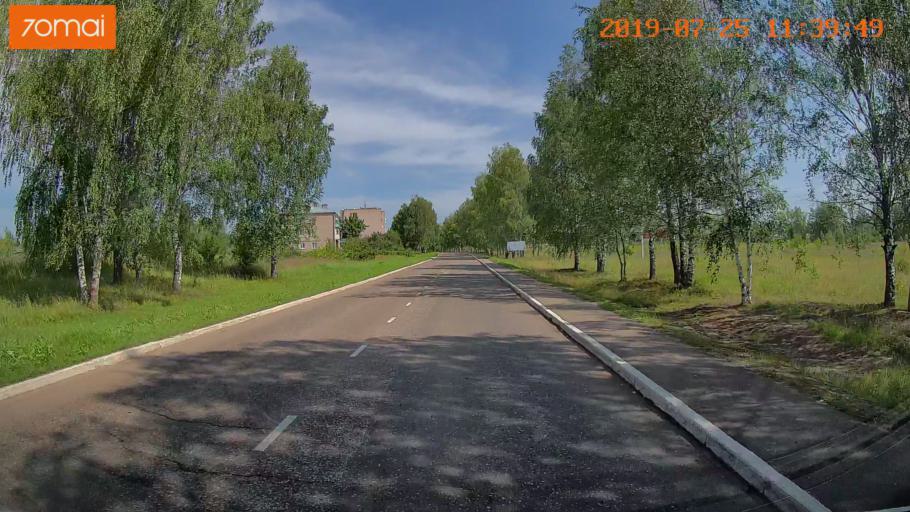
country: RU
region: Ivanovo
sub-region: Privolzhskiy Rayon
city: Ples
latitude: 57.4505
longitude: 41.5014
